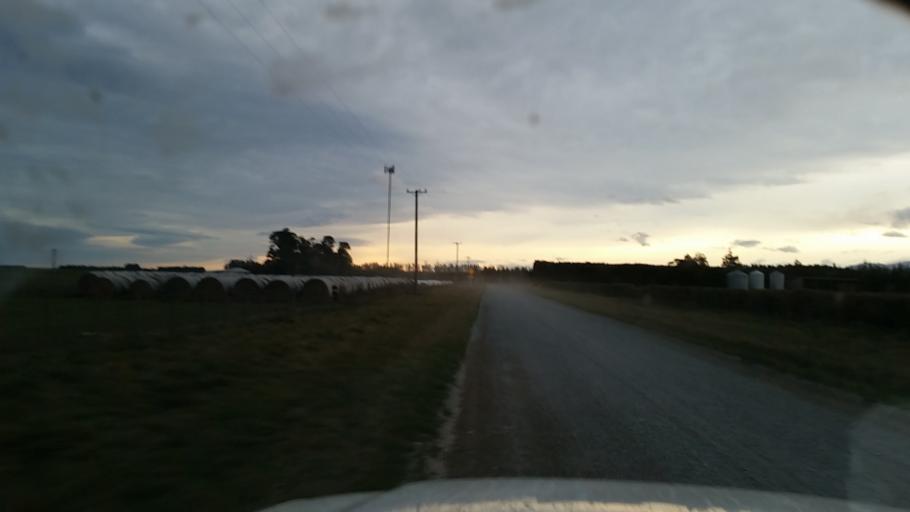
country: NZ
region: Canterbury
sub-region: Ashburton District
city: Tinwald
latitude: -43.8354
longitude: 171.6173
